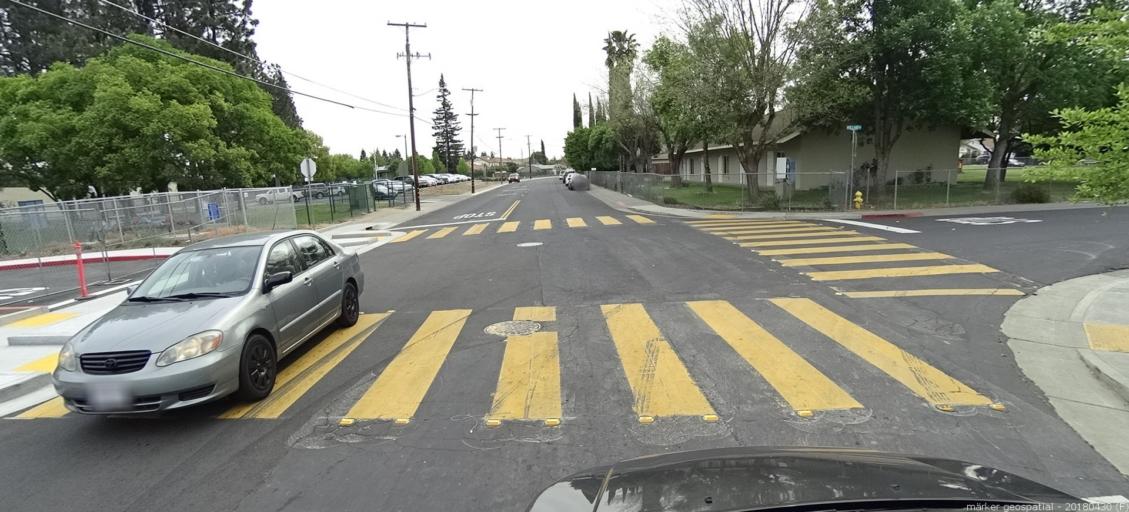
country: US
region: California
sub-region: Yolo County
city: West Sacramento
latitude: 38.5993
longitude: -121.5315
